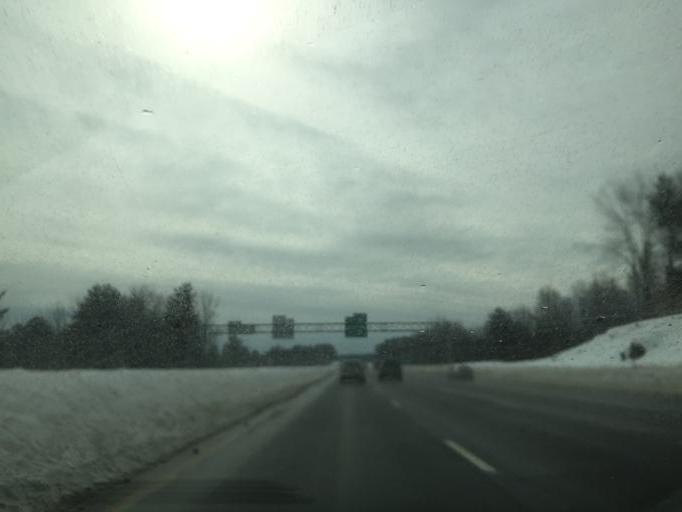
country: US
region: New Hampshire
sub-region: Strafford County
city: Rochester
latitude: 43.3086
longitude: -70.9957
